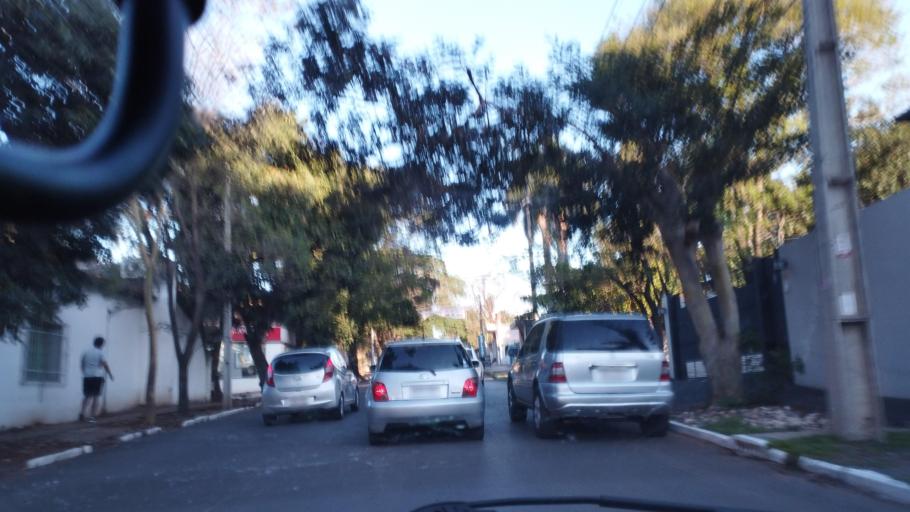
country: PY
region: Asuncion
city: Asuncion
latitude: -25.3020
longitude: -57.5873
